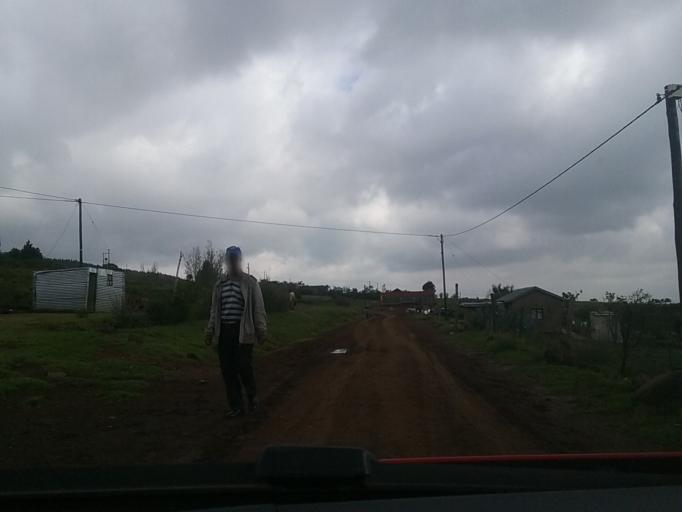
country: LS
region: Berea
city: Teyateyaneng
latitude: -29.2513
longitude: 27.8463
